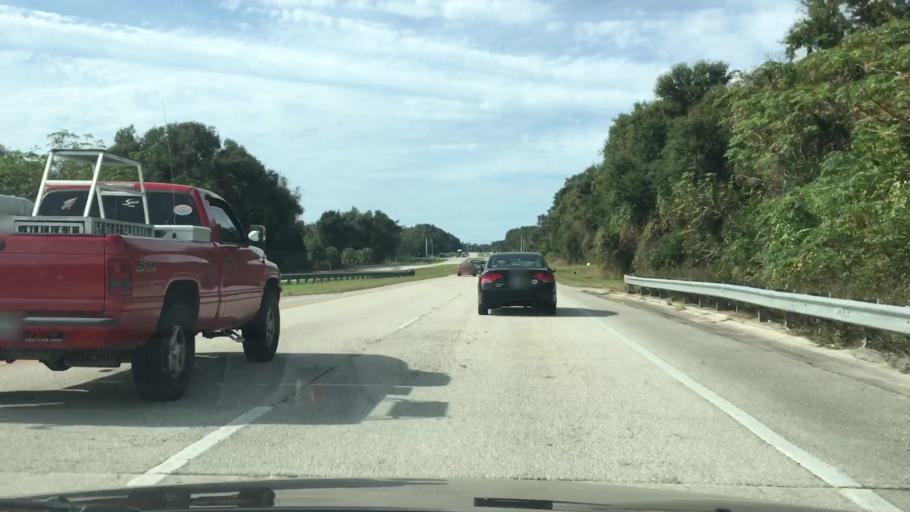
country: US
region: Florida
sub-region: Volusia County
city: North DeLand
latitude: 29.0547
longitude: -81.3120
